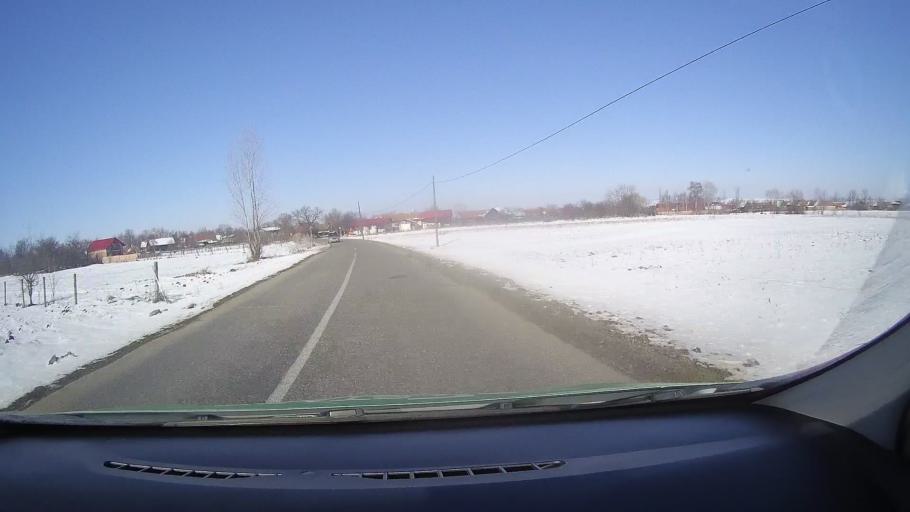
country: RO
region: Brasov
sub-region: Comuna Harseni
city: Harseni
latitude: 45.7838
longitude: 25.0011
